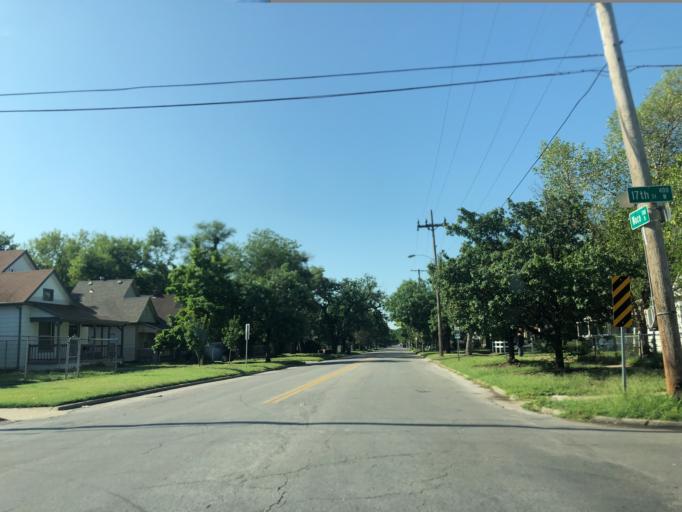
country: US
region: Kansas
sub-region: Sedgwick County
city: Wichita
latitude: 37.7156
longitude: -97.3420
